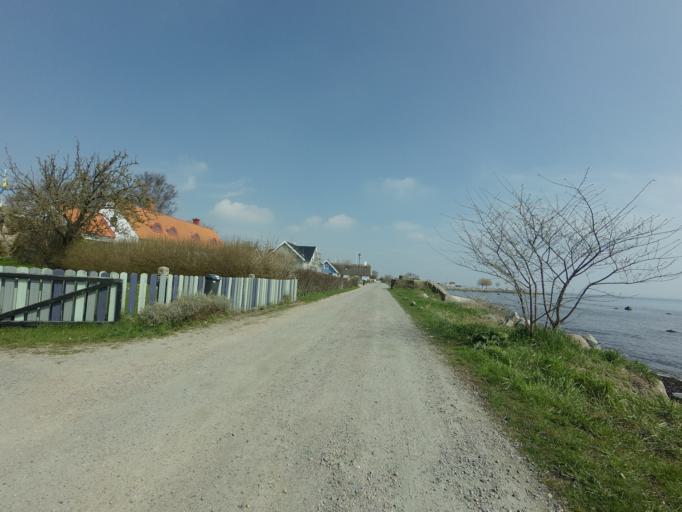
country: SE
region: Skane
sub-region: Skurups Kommun
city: Skivarp
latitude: 55.3922
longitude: 13.5989
